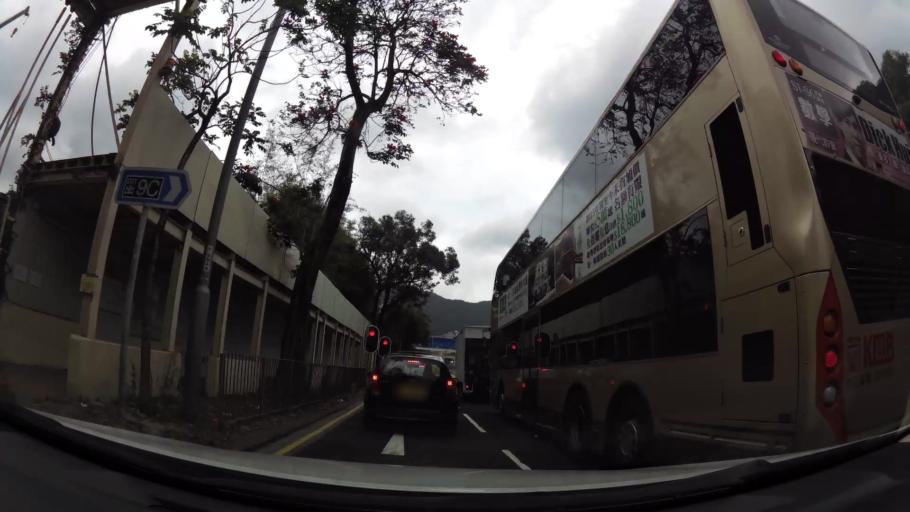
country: HK
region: Wong Tai Sin
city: Wong Tai Sin
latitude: 22.3339
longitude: 114.1788
